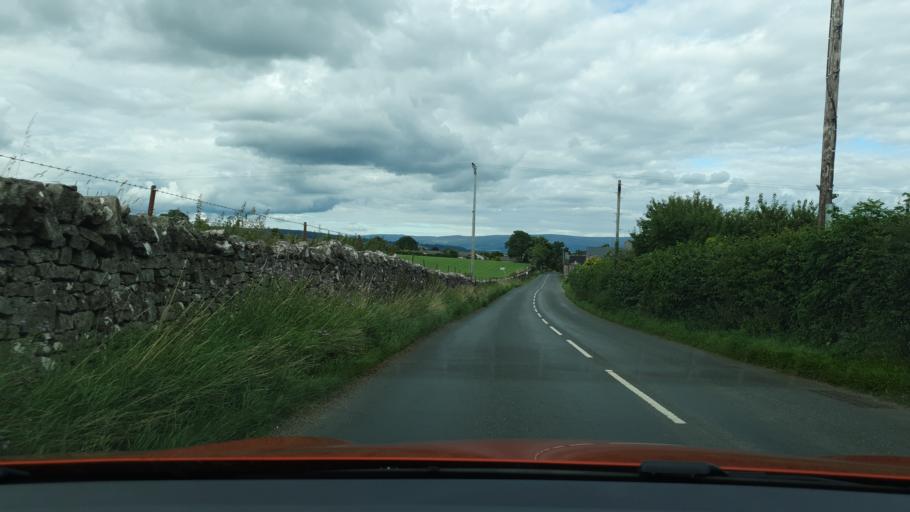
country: GB
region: England
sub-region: Cumbria
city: Penrith
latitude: 54.6298
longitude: -2.7807
